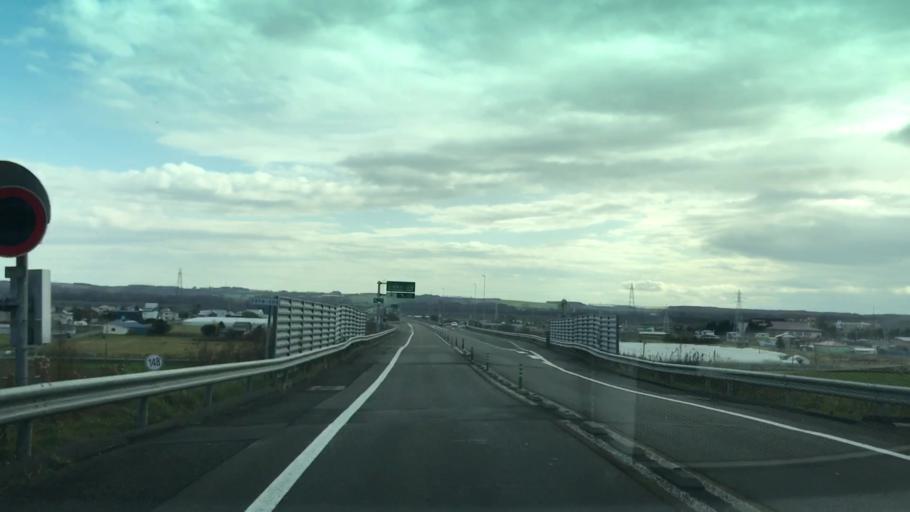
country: JP
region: Hokkaido
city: Shizunai-furukawacho
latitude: 42.5313
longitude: 142.0329
